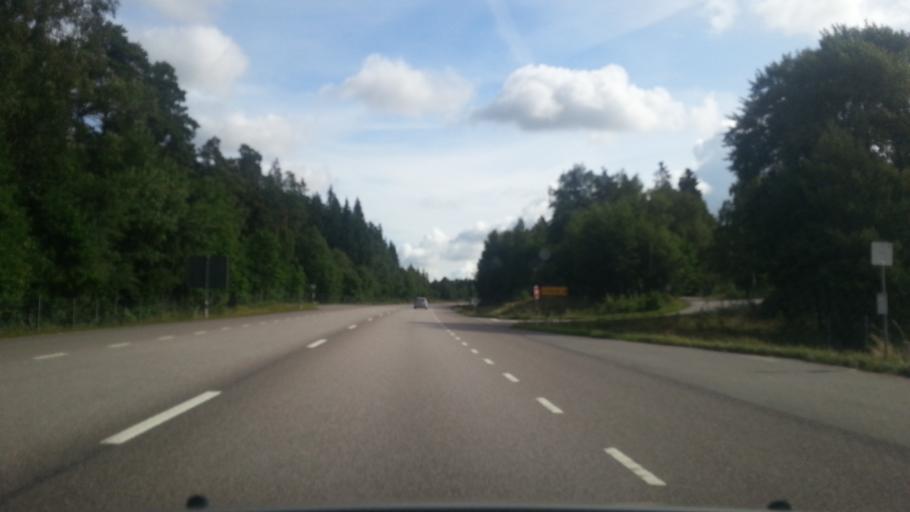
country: SE
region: Vaestra Goetaland
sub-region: Vanersborgs Kommun
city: Vargon
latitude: 58.2999
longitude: 12.5098
